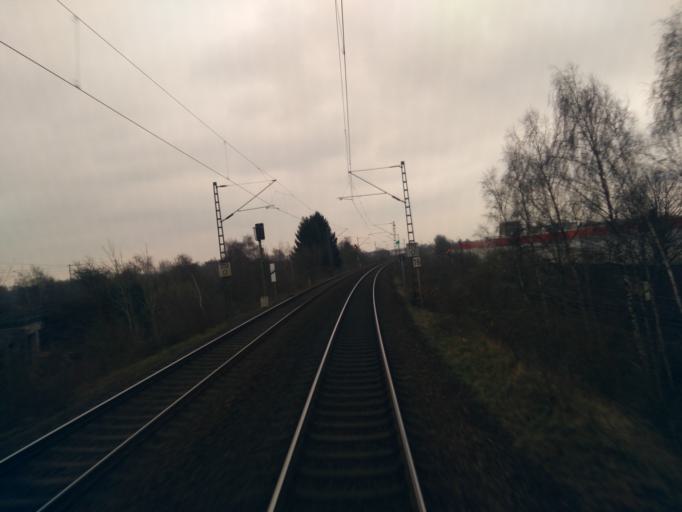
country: DE
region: Bremen
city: Bremen
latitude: 53.0747
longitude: 8.8596
